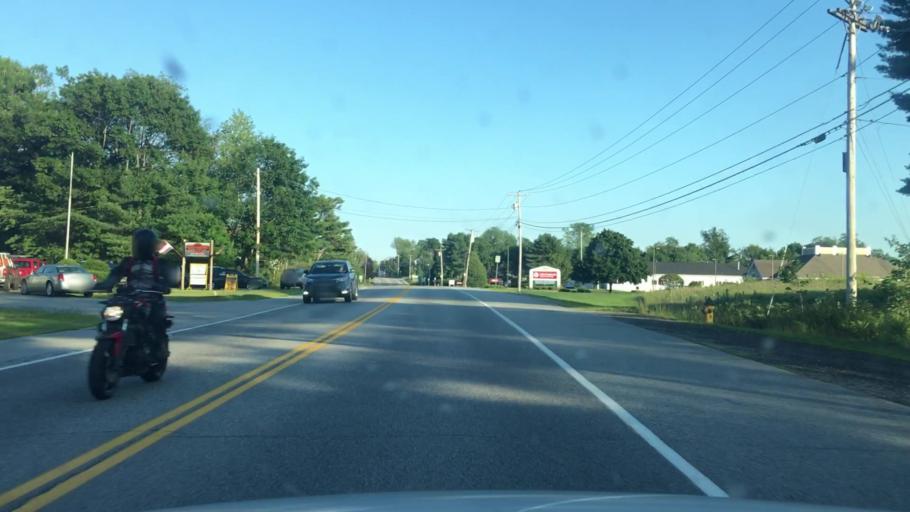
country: US
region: Maine
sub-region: Androscoggin County
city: Lisbon
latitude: 44.0246
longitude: -70.0998
